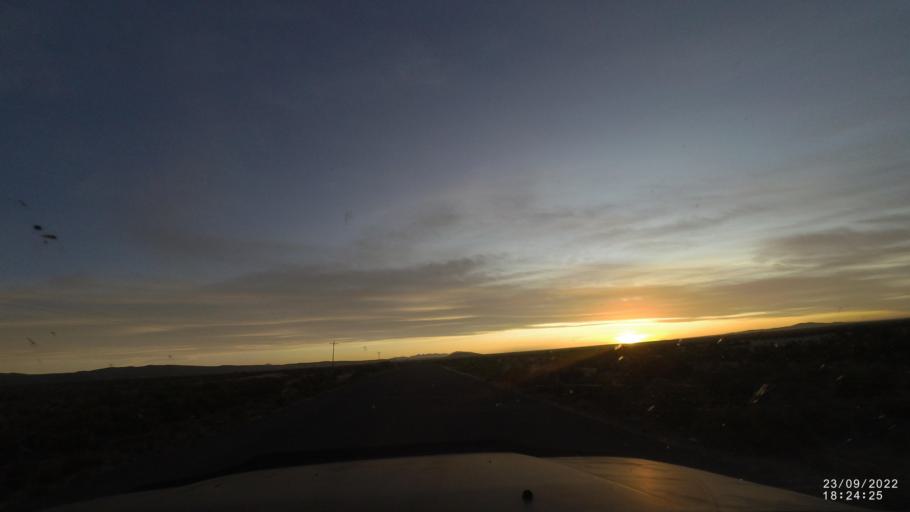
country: BO
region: Oruro
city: Challapata
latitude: -19.3026
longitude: -67.1204
